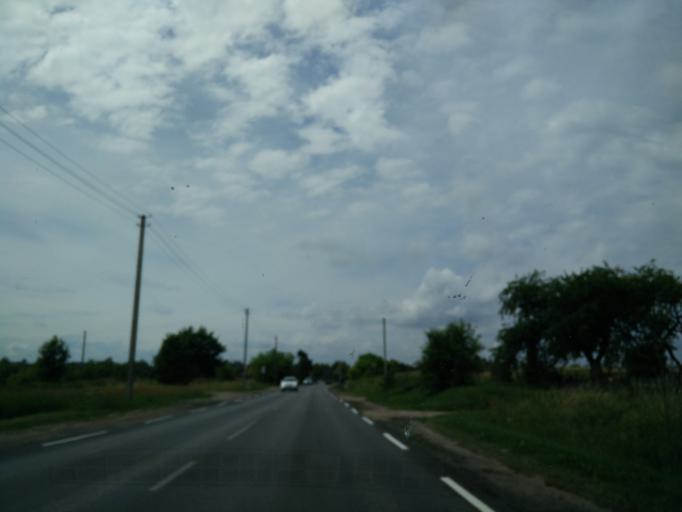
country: LT
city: Skaidiskes
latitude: 54.6922
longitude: 25.4615
